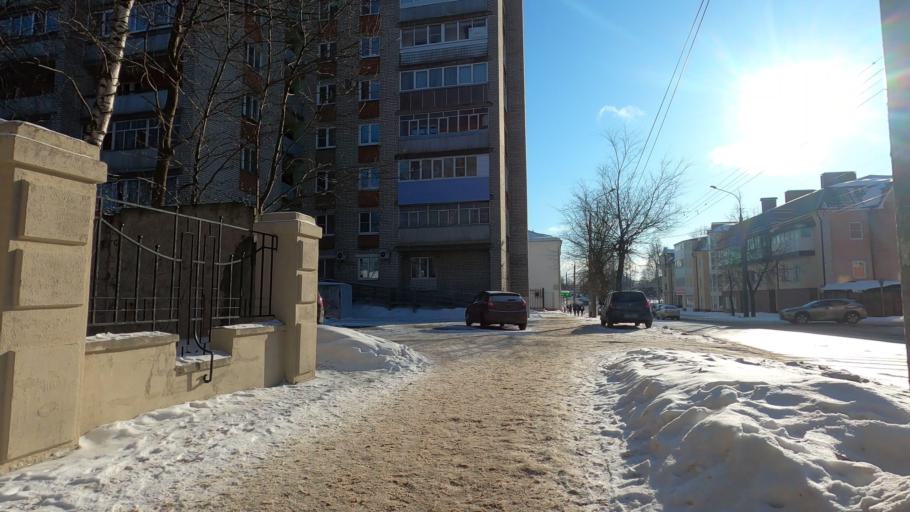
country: RU
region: Jaroslavl
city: Rybinsk
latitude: 58.0461
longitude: 38.8387
